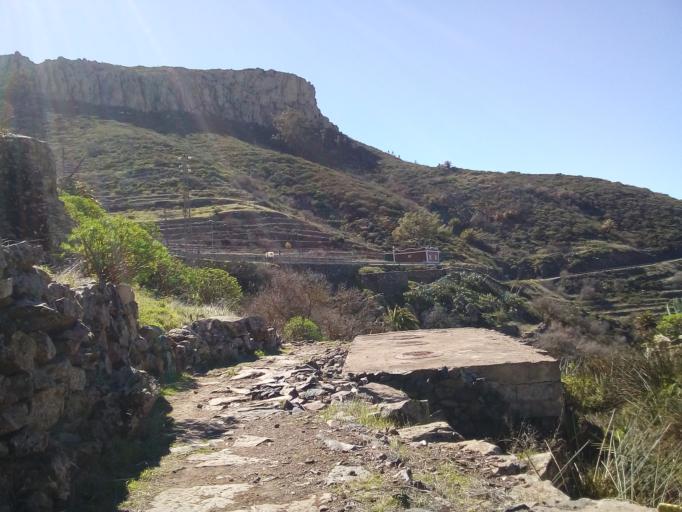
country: ES
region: Canary Islands
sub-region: Provincia de Santa Cruz de Tenerife
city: Alajero
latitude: 28.1049
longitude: -17.2749
